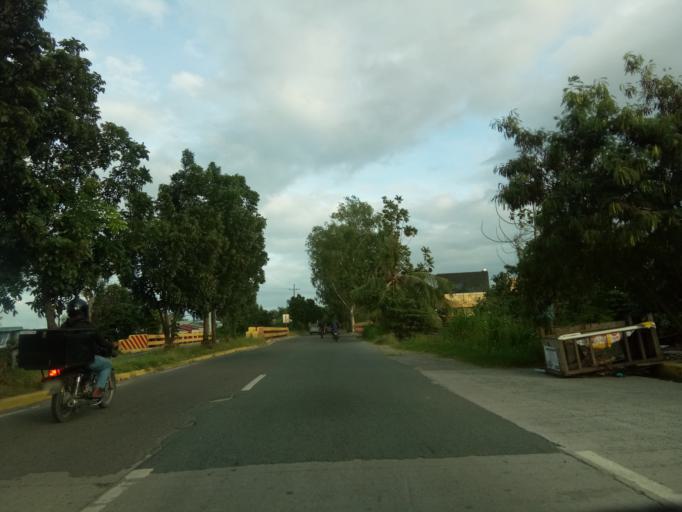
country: PH
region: Calabarzon
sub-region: Province of Cavite
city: Imus
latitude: 14.3887
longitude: 120.9688
